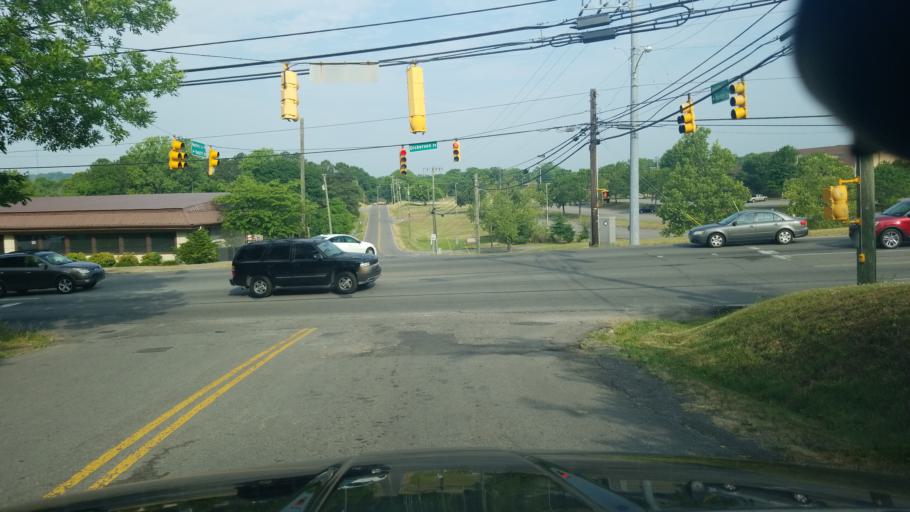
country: US
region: Tennessee
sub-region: Davidson County
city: Goodlettsville
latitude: 36.2776
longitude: -86.7509
